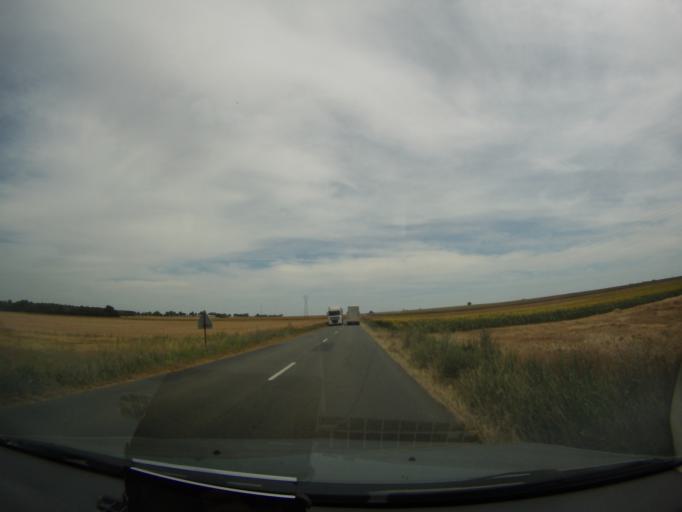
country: FR
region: Poitou-Charentes
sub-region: Departement de la Vienne
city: Mirebeau
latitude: 46.7268
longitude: 0.1992
